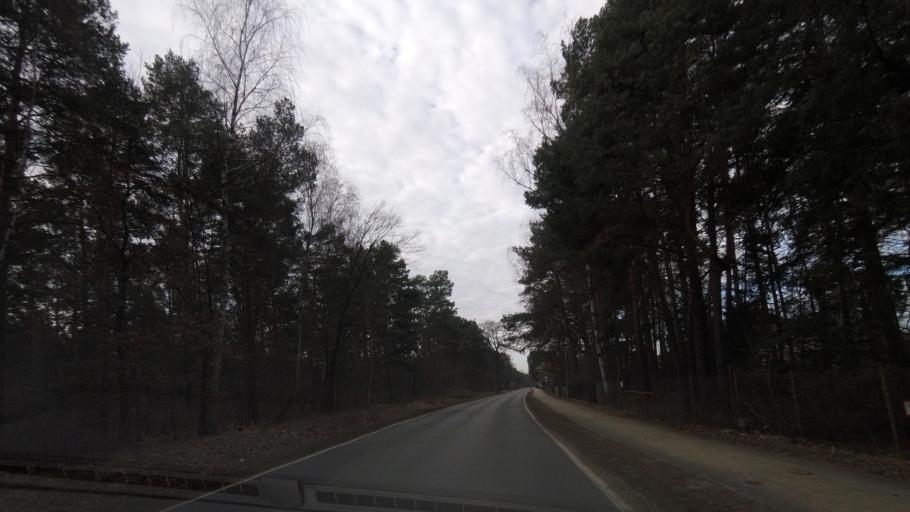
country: DE
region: Berlin
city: Schmockwitz
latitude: 52.3555
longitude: 13.6753
